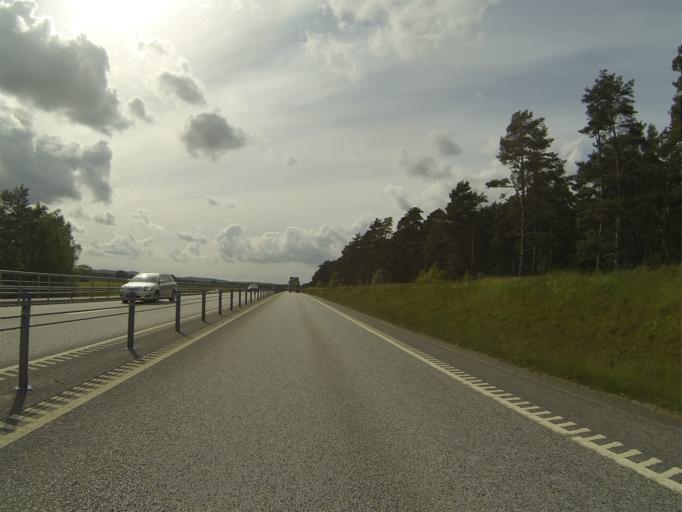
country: SE
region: Skane
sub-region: Sjobo Kommun
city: Blentarp
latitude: 55.6390
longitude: 13.5645
